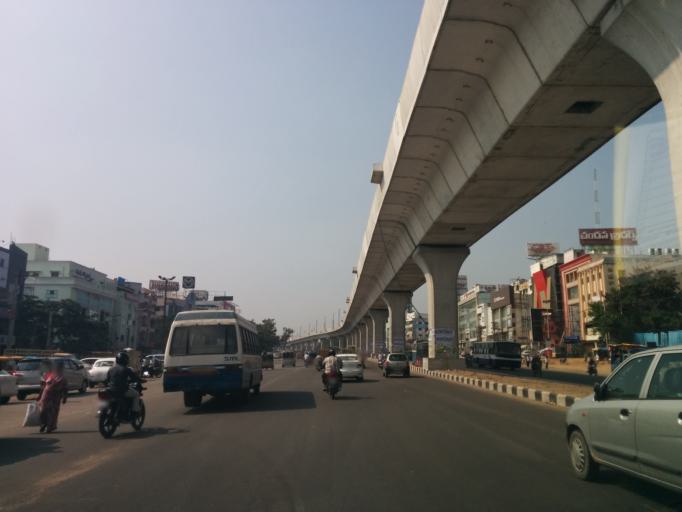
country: IN
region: Telangana
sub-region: Rangareddi
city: Kukatpalli
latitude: 17.4946
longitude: 78.3997
